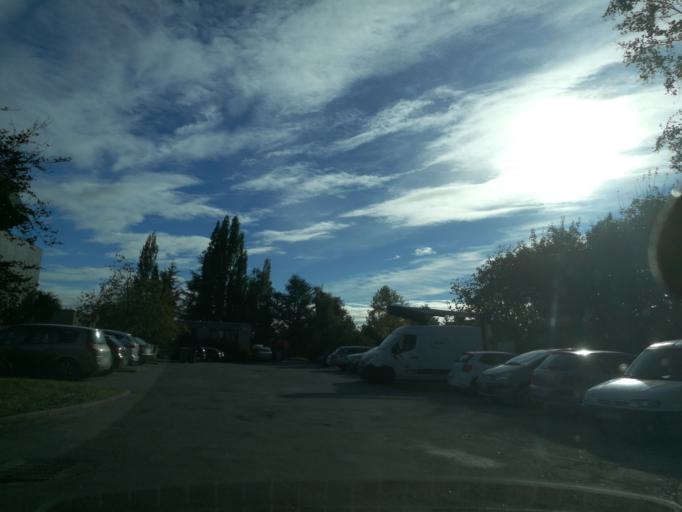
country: FR
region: Brittany
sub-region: Departement d'Ille-et-Vilaine
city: Montauban-de-Bretagne
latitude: 48.1976
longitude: -2.0421
